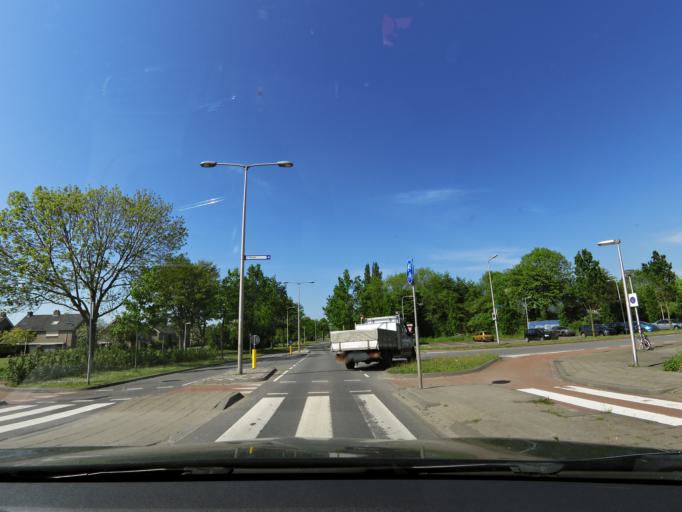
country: NL
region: South Holland
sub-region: Gemeente Albrandswaard
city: Rhoon
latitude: 51.8563
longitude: 4.4339
